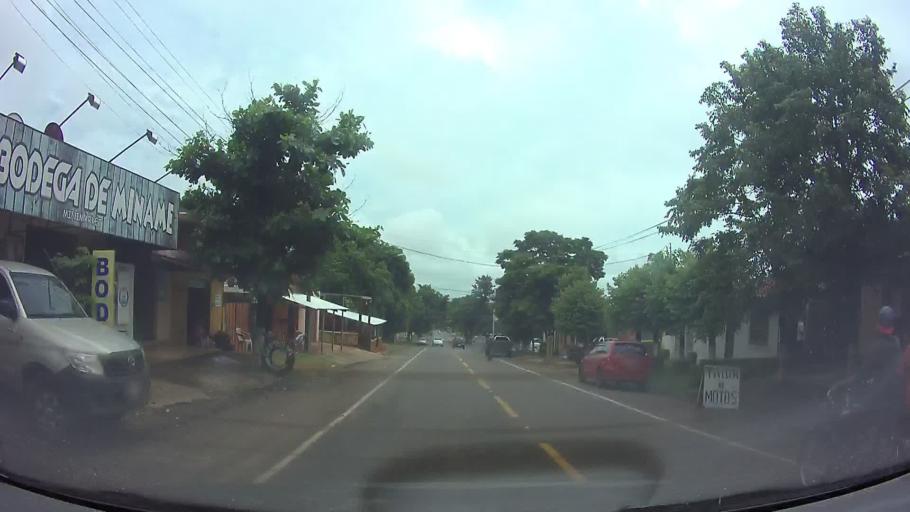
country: PY
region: Paraguari
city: Acahay
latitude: -25.9105
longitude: -57.1147
